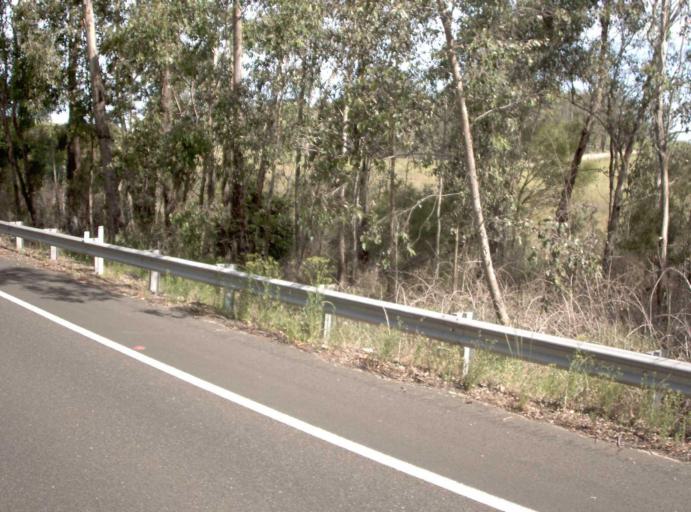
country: AU
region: Victoria
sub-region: East Gippsland
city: Lakes Entrance
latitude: -37.8260
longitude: 147.8901
